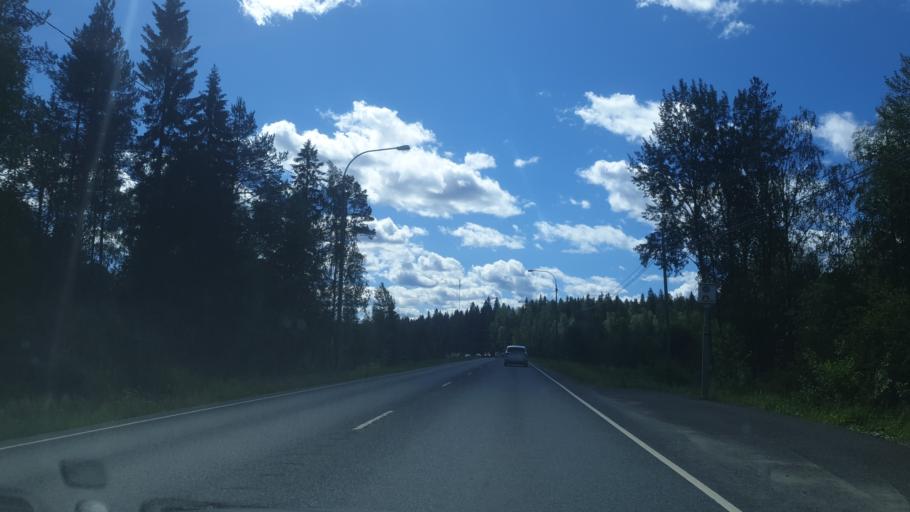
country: FI
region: Northern Savo
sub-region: Varkaus
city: Leppaevirta
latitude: 62.5596
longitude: 27.6206
